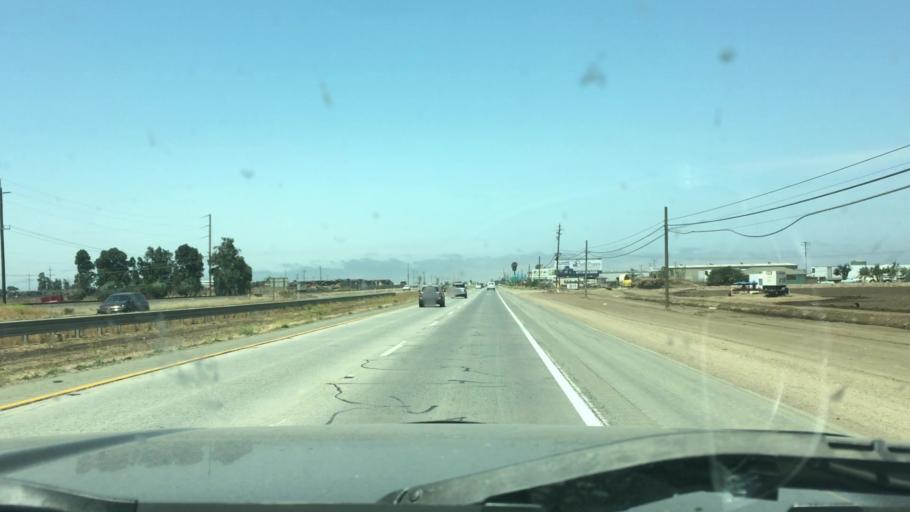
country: US
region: California
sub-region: Monterey County
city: Chualar
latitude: 36.6085
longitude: -121.5609
